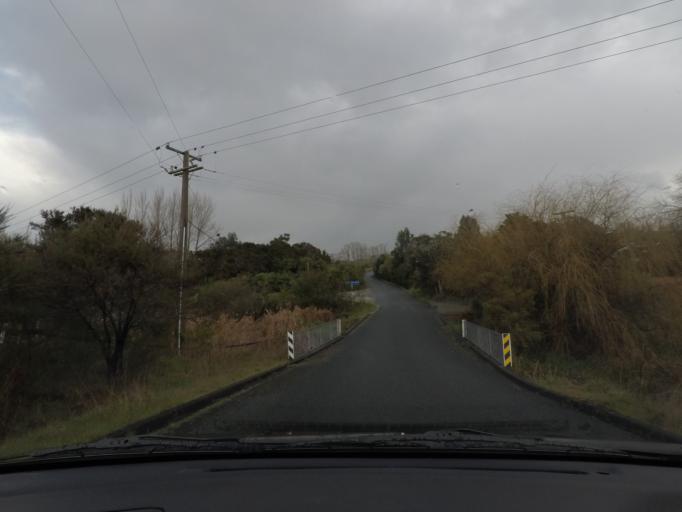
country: NZ
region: Auckland
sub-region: Auckland
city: Warkworth
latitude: -36.4328
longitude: 174.7310
